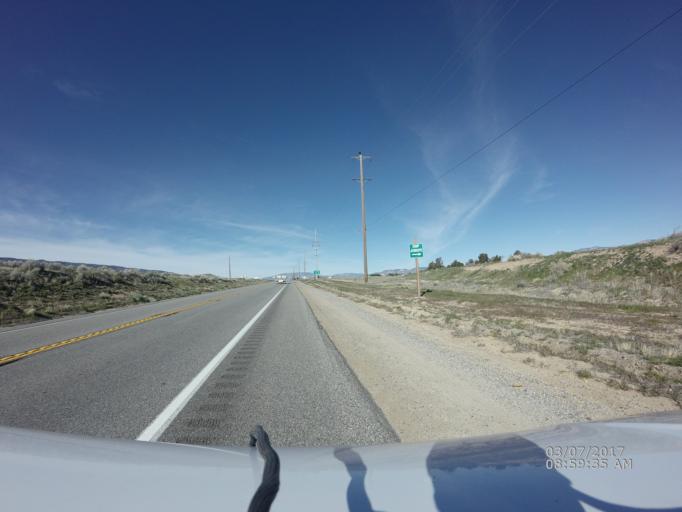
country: US
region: California
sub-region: Los Angeles County
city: Green Valley
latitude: 34.7757
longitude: -118.5734
